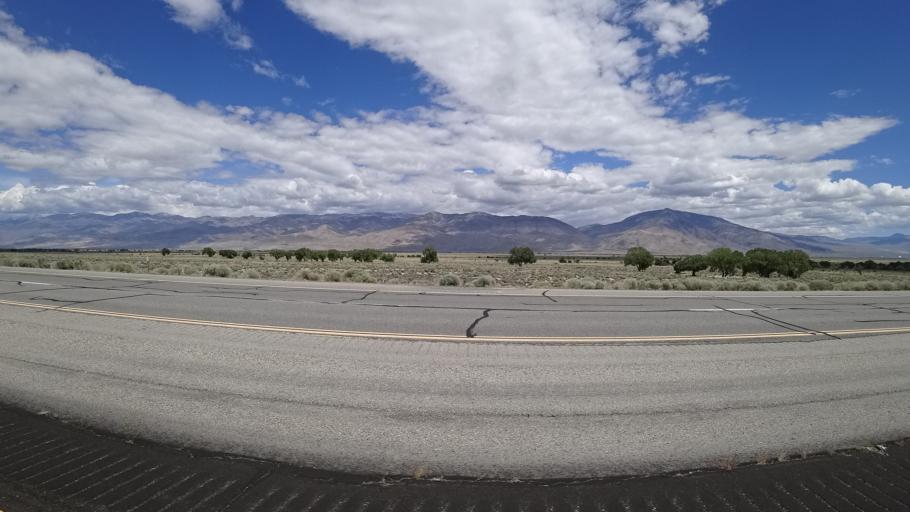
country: US
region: California
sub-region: Inyo County
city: Bishop
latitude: 37.2942
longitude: -118.3752
